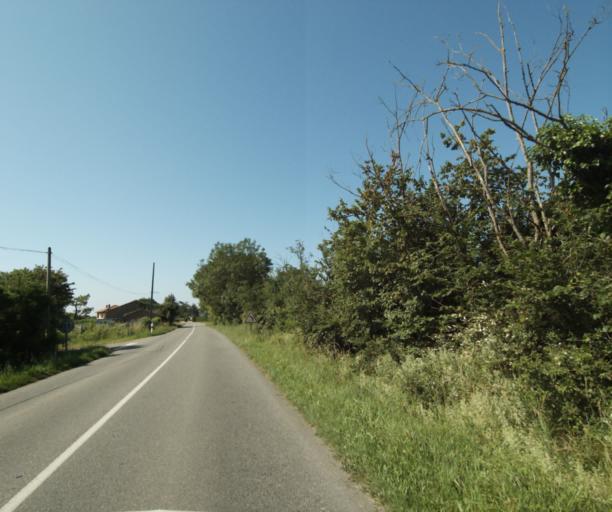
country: FR
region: Midi-Pyrenees
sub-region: Departement du Tarn-et-Garonne
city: Bressols
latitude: 43.9720
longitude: 1.3576
